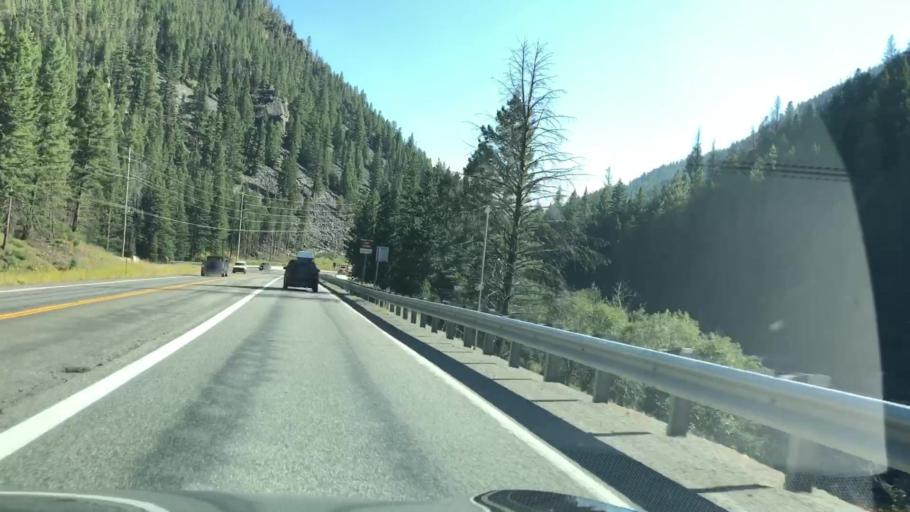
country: US
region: Montana
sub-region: Gallatin County
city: Big Sky
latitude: 45.3735
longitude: -111.1756
